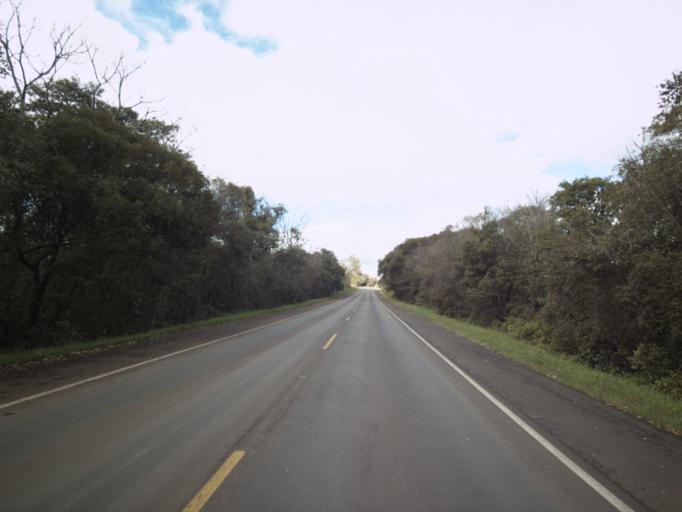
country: BR
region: Santa Catarina
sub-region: Concordia
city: Concordia
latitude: -27.3311
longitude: -51.9774
